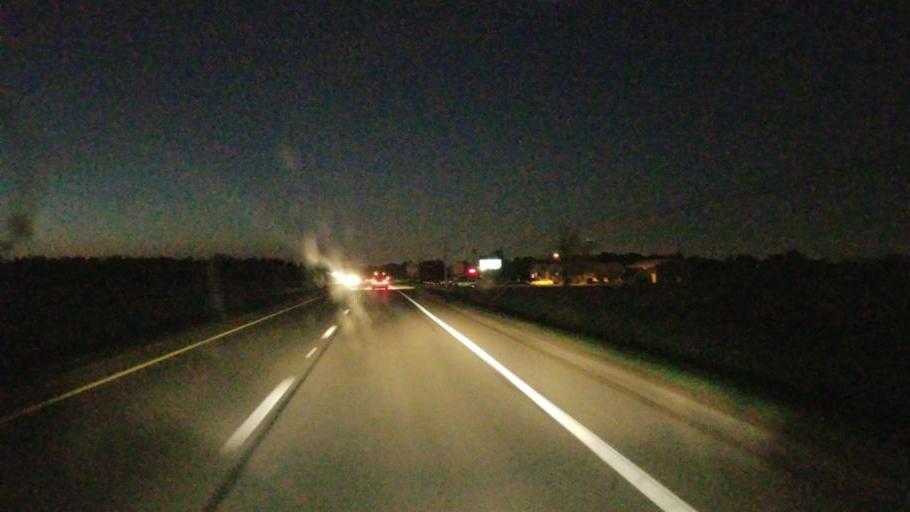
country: US
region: Ohio
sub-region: Pickaway County
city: Ashville
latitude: 39.6721
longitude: -82.9670
